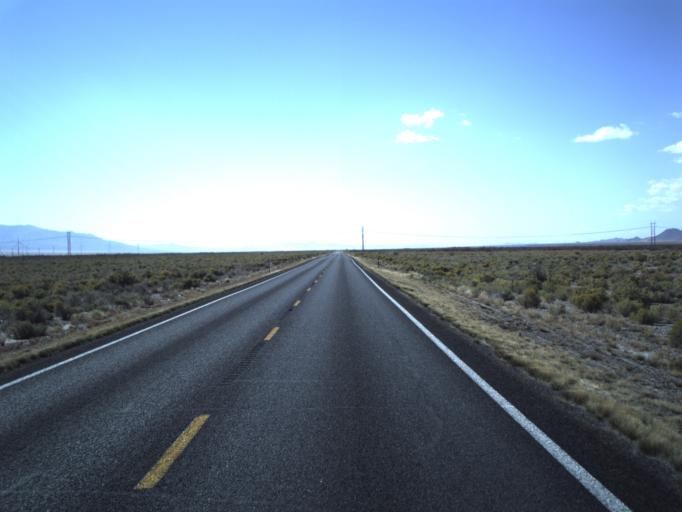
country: US
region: Utah
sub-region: Beaver County
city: Milford
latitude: 38.5818
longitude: -112.9890
